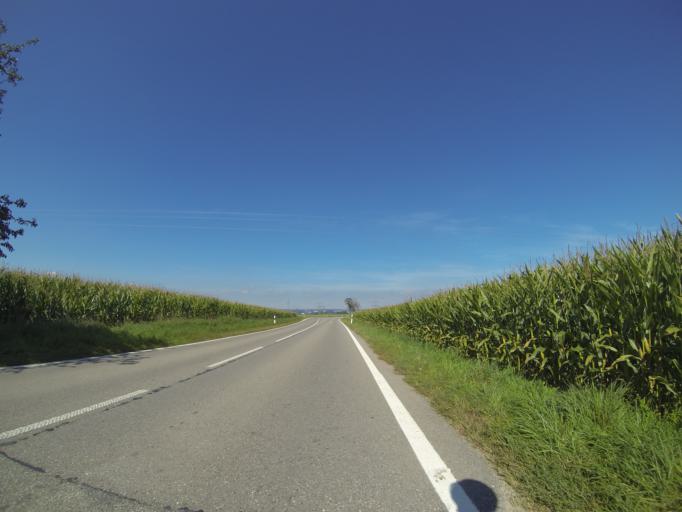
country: DE
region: Baden-Wuerttemberg
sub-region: Tuebingen Region
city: Achstetten
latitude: 48.2840
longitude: 9.9055
